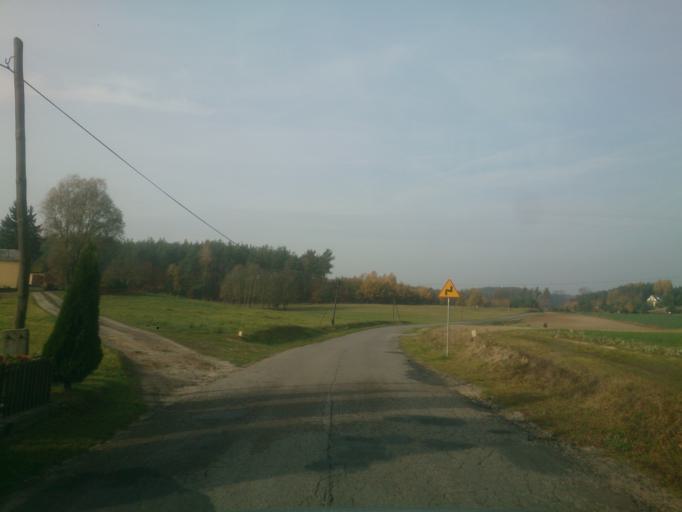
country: PL
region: Kujawsko-Pomorskie
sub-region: Powiat brodnicki
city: Brodnica
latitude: 53.3350
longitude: 19.3600
